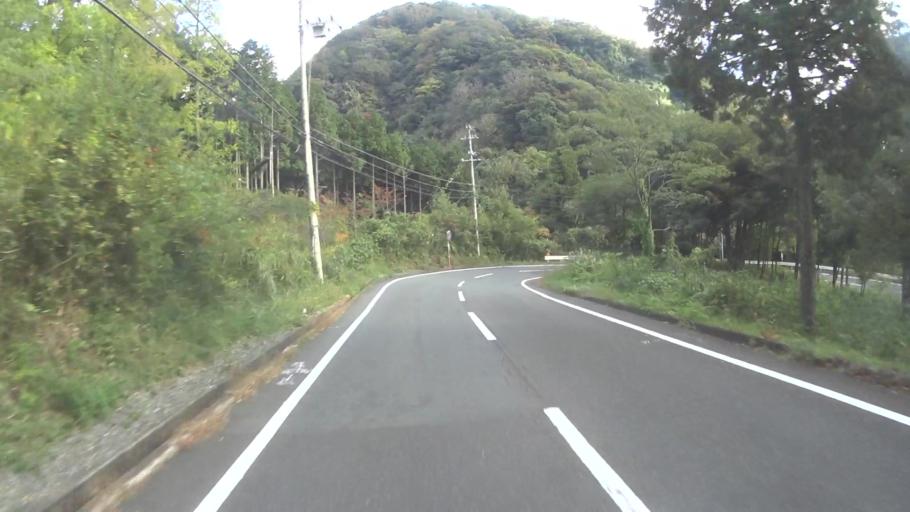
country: JP
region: Kyoto
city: Maizuru
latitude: 35.5329
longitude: 135.3946
